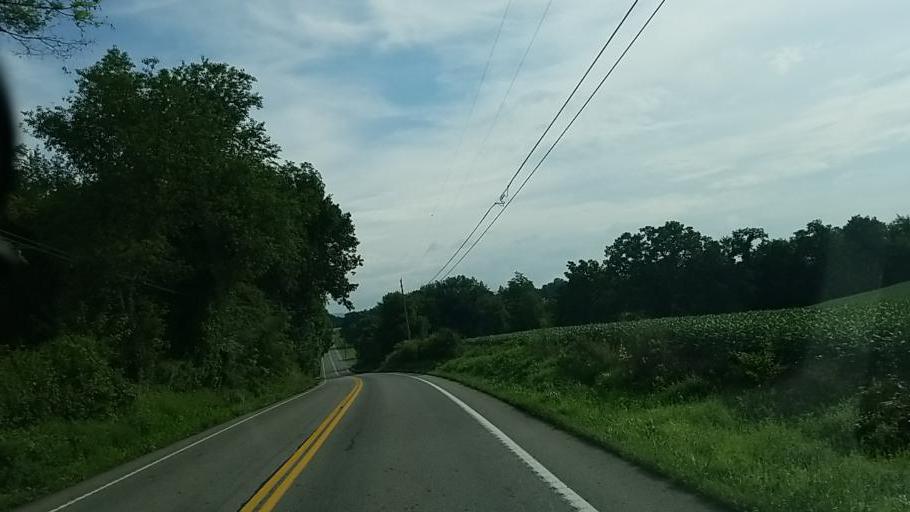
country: US
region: Pennsylvania
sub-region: Dauphin County
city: Millersburg
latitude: 40.5709
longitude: -76.9097
